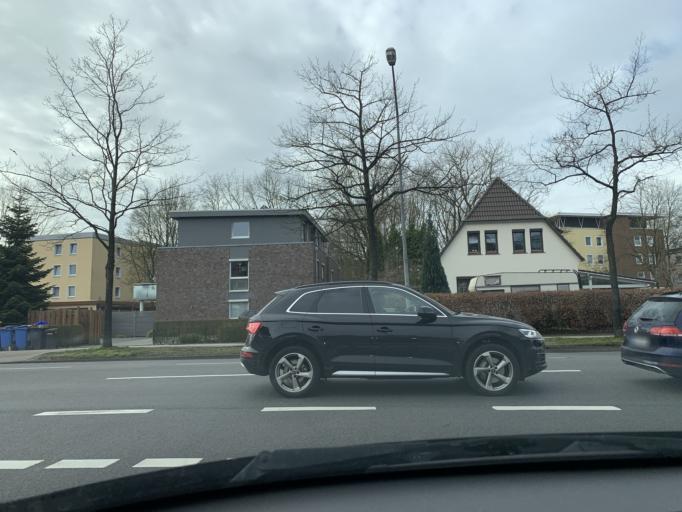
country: DE
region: Lower Saxony
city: Oldenburg
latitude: 53.1240
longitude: 8.1916
